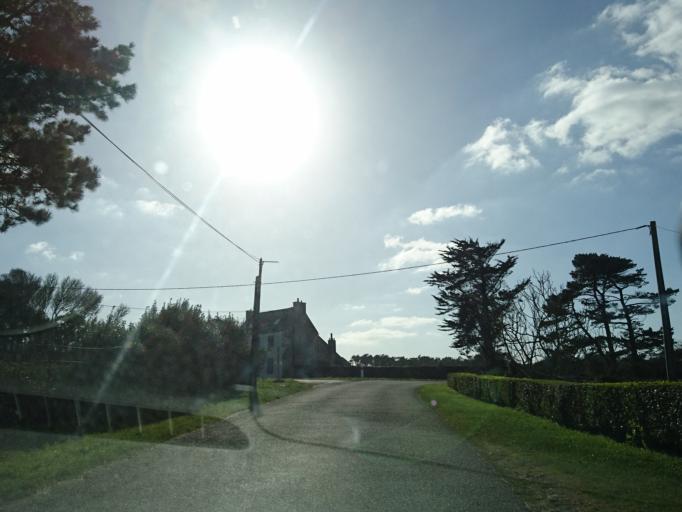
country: FR
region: Brittany
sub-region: Departement du Finistere
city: Roscanvel
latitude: 48.3248
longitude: -4.5710
